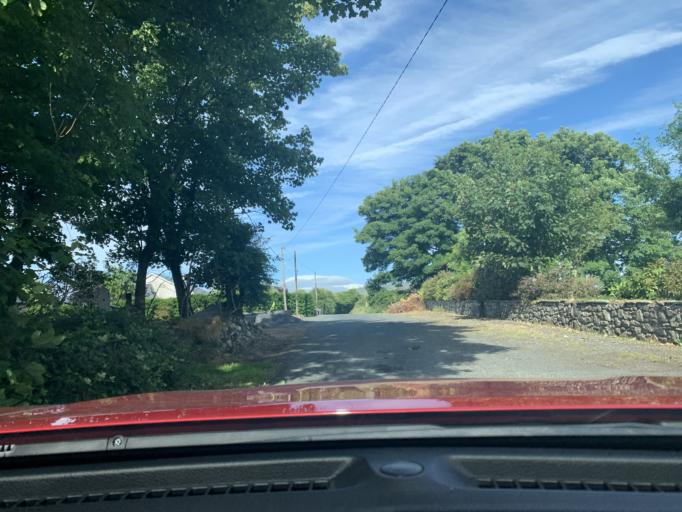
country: IE
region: Connaught
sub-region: Sligo
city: Sligo
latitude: 54.2551
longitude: -8.5073
